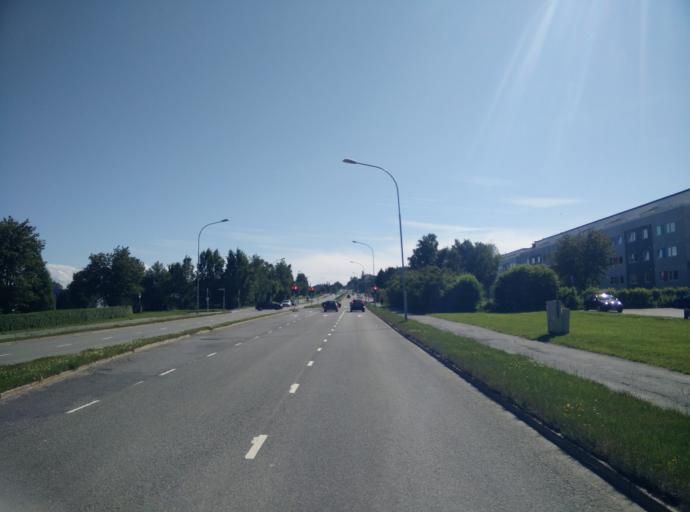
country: NO
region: Sor-Trondelag
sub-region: Trondheim
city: Trondheim
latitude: 63.4100
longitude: 10.3604
